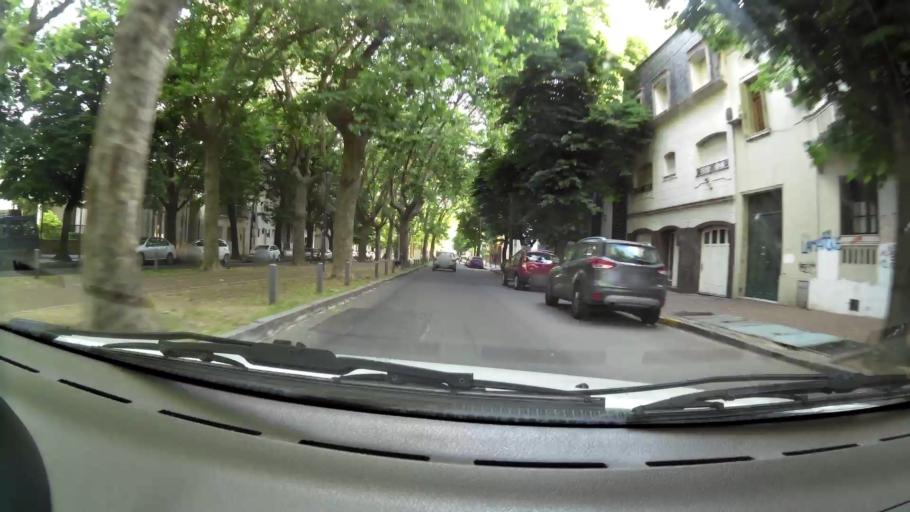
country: AR
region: Buenos Aires
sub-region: Partido de La Plata
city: La Plata
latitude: -34.9192
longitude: -57.9511
